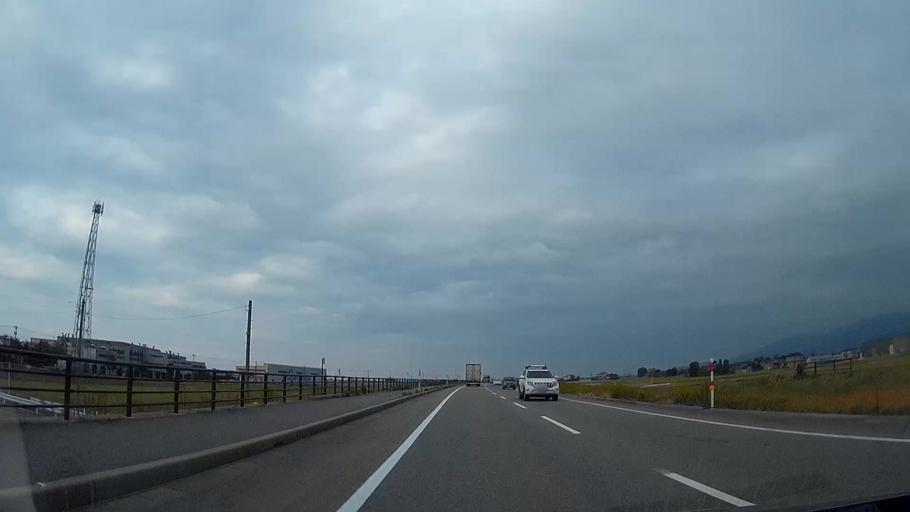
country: JP
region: Toyama
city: Nyuzen
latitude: 36.9227
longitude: 137.4694
